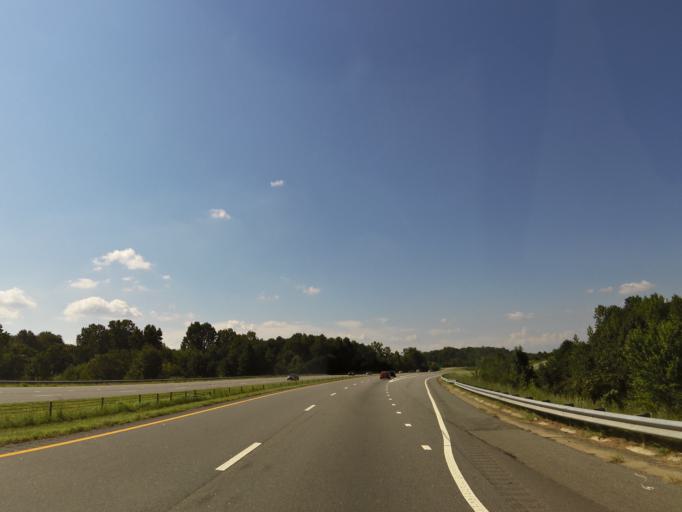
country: US
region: North Carolina
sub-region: Catawba County
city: Mountain View
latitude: 35.6888
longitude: -81.3491
